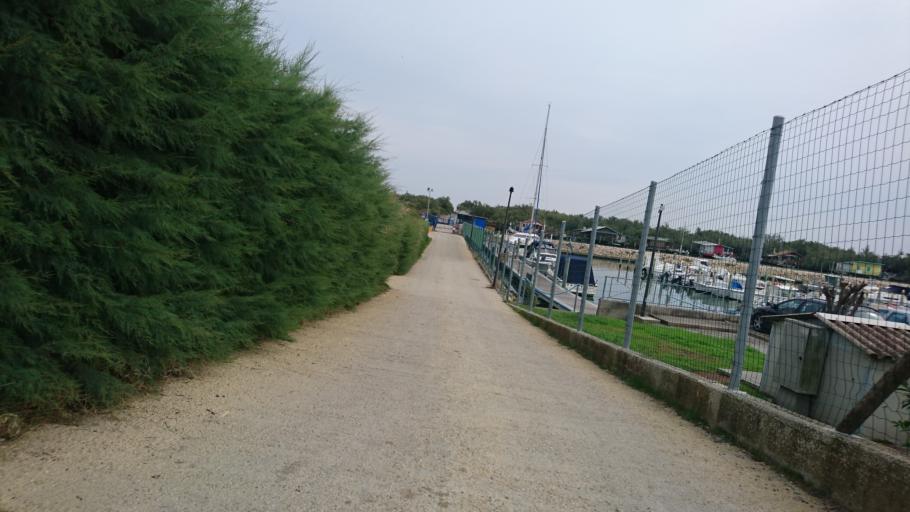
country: IT
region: Veneto
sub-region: Provincia di Rovigo
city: Scardovari
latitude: 44.8494
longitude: 12.4640
